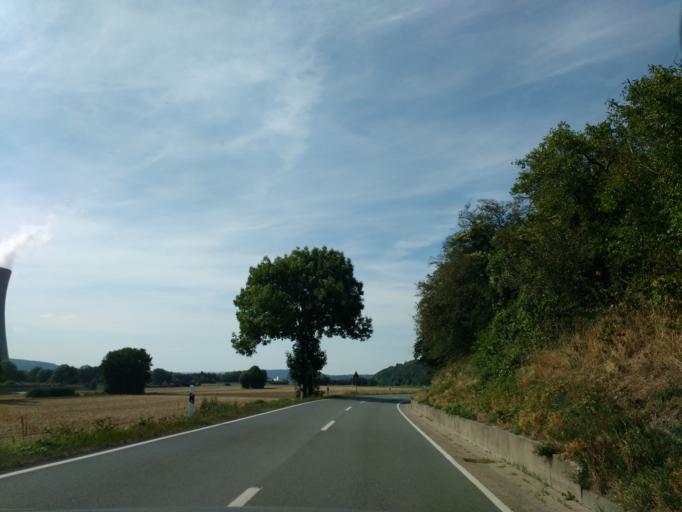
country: DE
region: Lower Saxony
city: Hehlen
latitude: 52.0355
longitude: 9.4255
